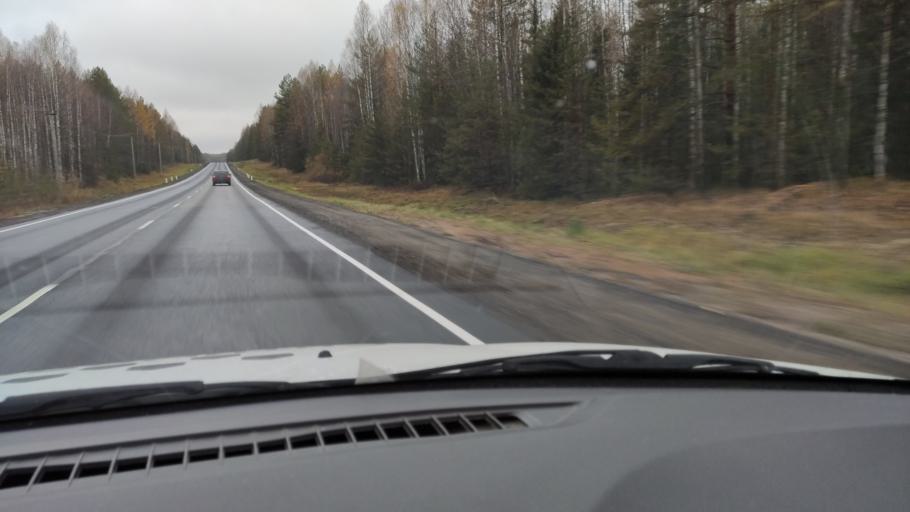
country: RU
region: Kirov
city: Belaya Kholunitsa
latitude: 58.9158
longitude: 51.1494
